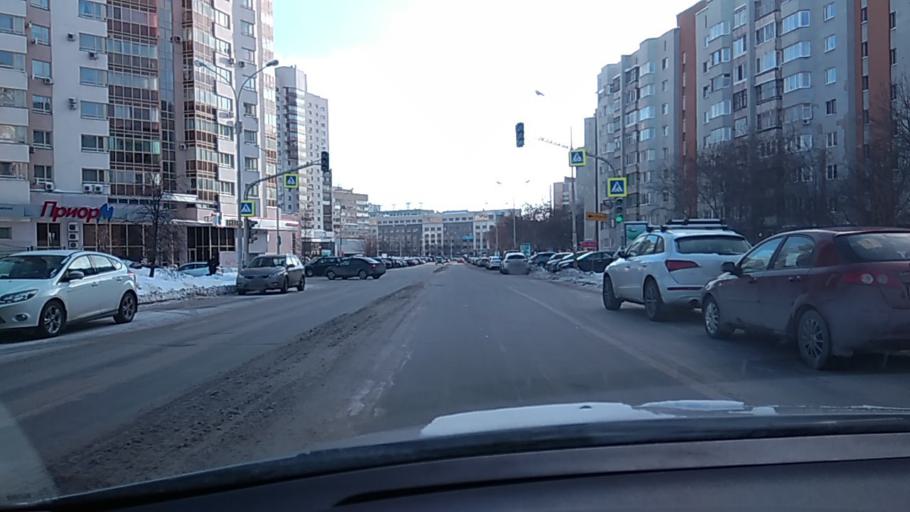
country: RU
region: Sverdlovsk
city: Yekaterinburg
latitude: 56.8411
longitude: 60.5870
